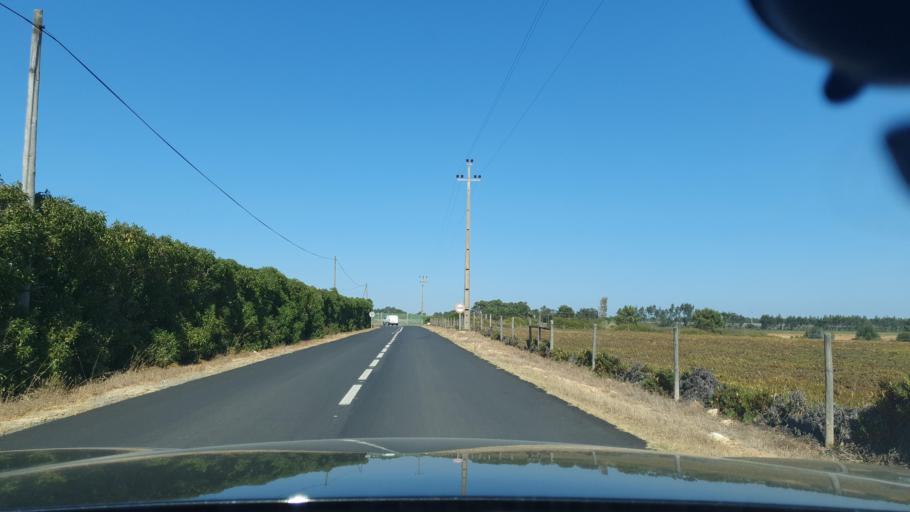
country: PT
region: Beja
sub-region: Odemira
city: Sao Teotonio
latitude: 37.4651
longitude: -8.7912
